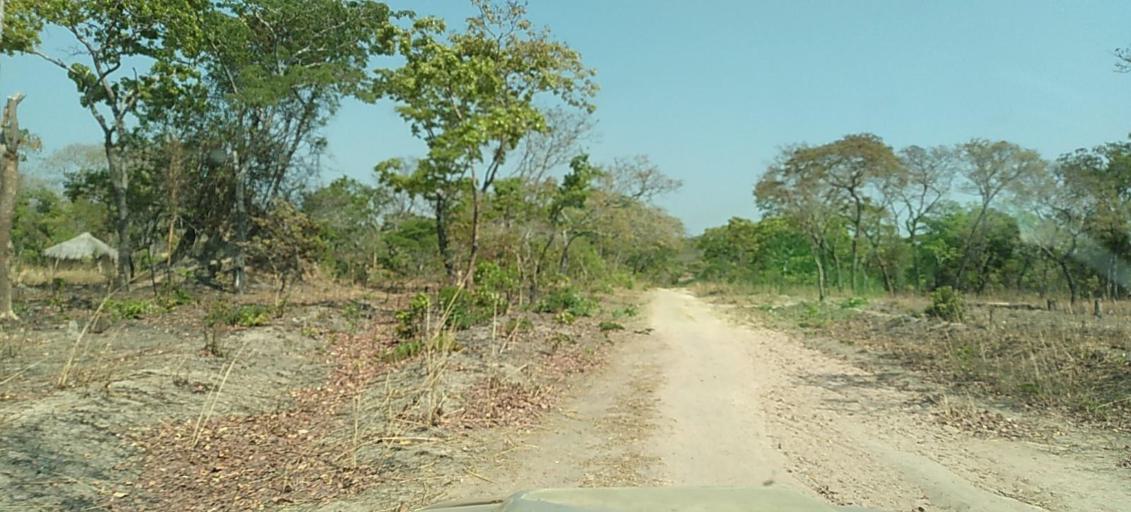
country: ZM
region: North-Western
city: Kalengwa
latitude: -13.3006
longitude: 24.7957
